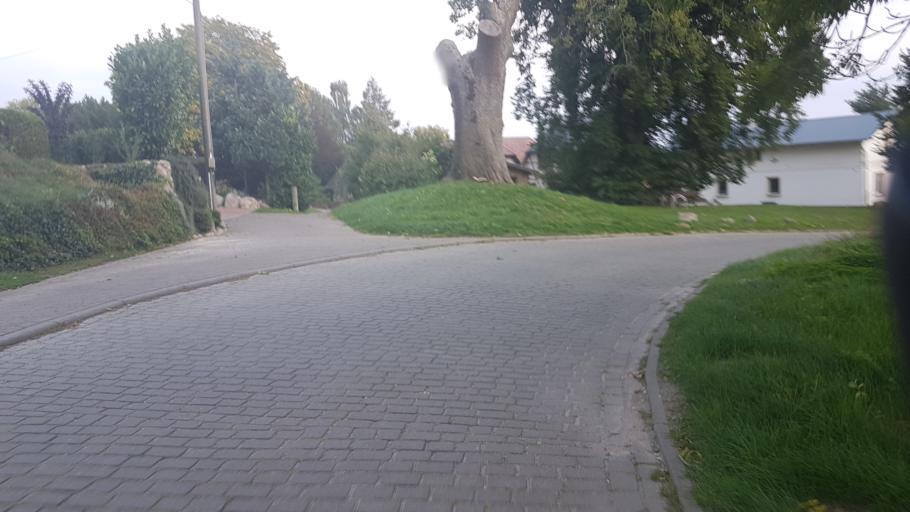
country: DE
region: Mecklenburg-Vorpommern
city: Putbus
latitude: 54.3561
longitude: 13.5142
